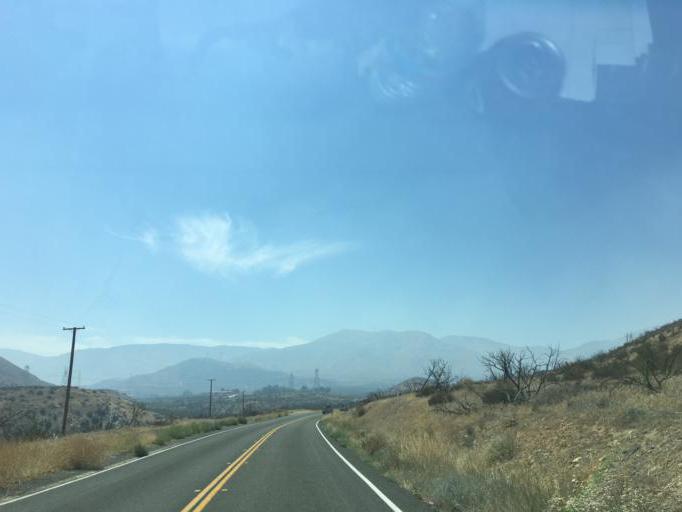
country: US
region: California
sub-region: Los Angeles County
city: Acton
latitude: 34.4490
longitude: -118.1529
